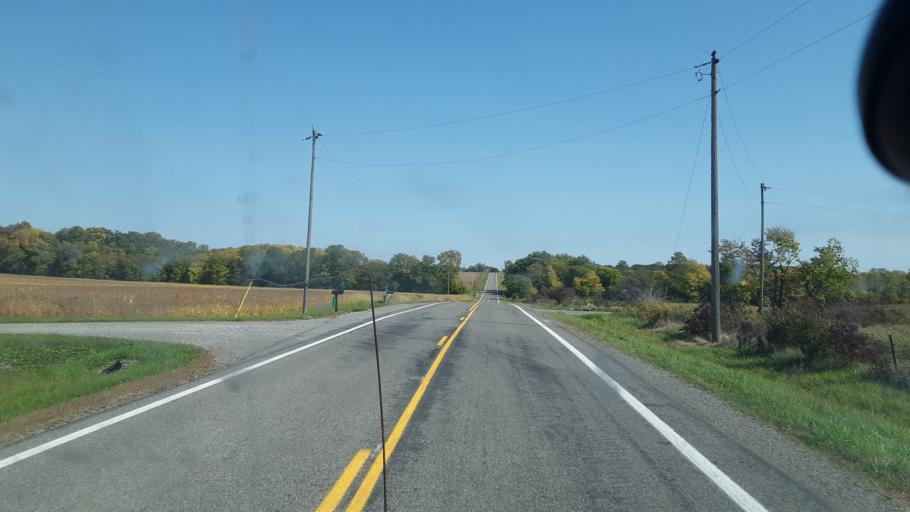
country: US
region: Ohio
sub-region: Logan County
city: Northwood
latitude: 40.5048
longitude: -83.6870
